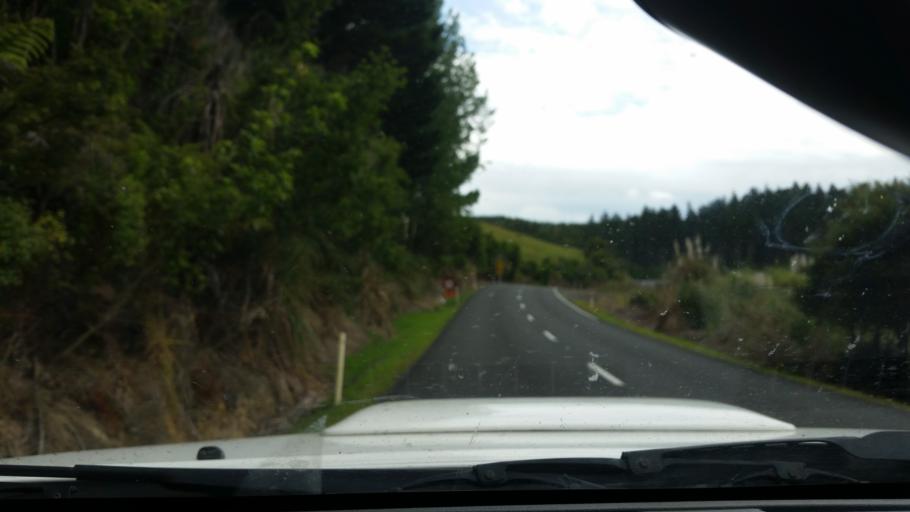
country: NZ
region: Northland
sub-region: Kaipara District
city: Dargaville
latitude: -35.7382
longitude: 173.8688
